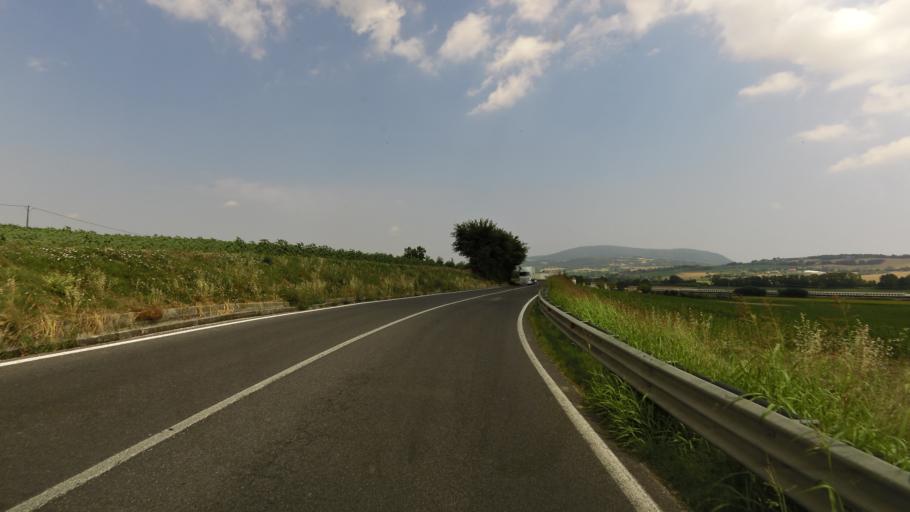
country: IT
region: The Marches
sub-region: Provincia di Ancona
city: Castelfidardo
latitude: 43.4818
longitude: 13.5783
